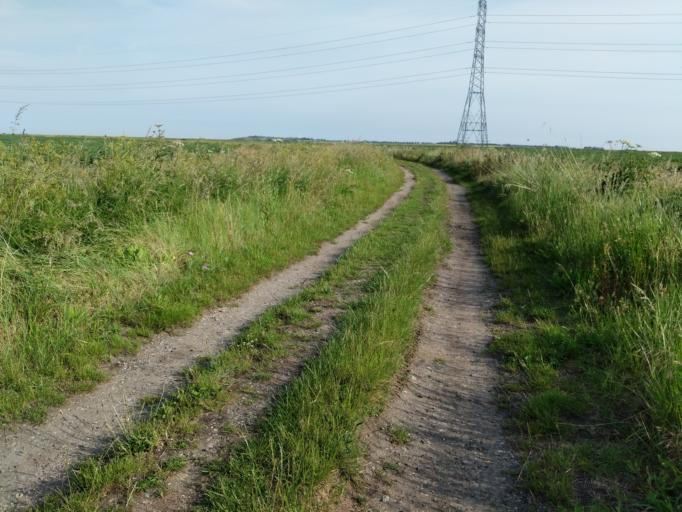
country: GB
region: England
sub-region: Kent
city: Faversham
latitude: 51.3363
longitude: 0.9151
